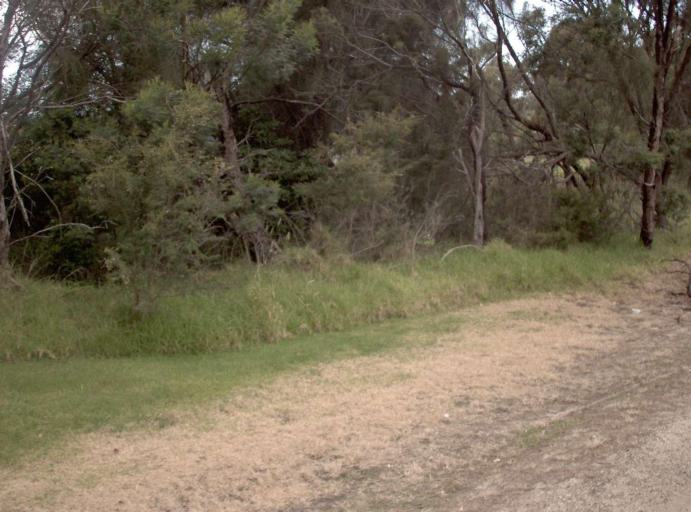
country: AU
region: Victoria
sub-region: Wellington
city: Sale
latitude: -38.1927
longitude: 147.0941
